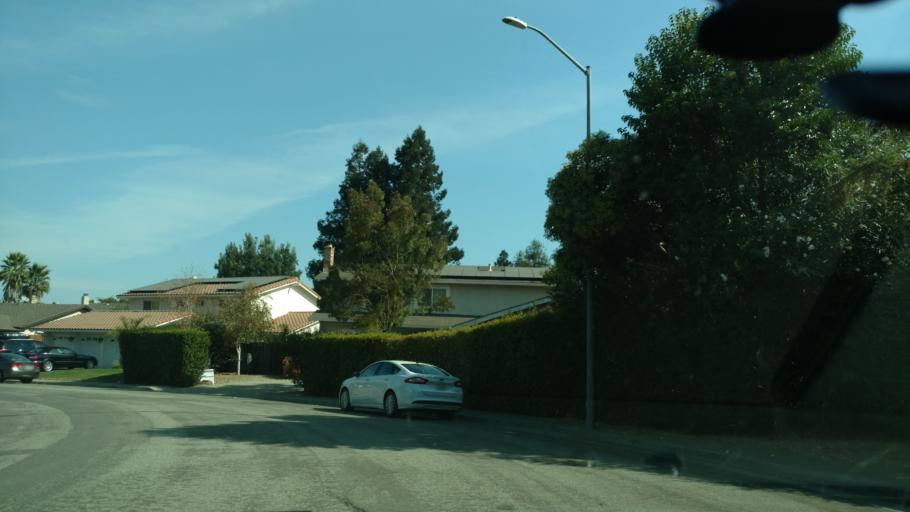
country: US
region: California
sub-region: Santa Clara County
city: Morgan Hill
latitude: 37.1010
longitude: -121.6432
